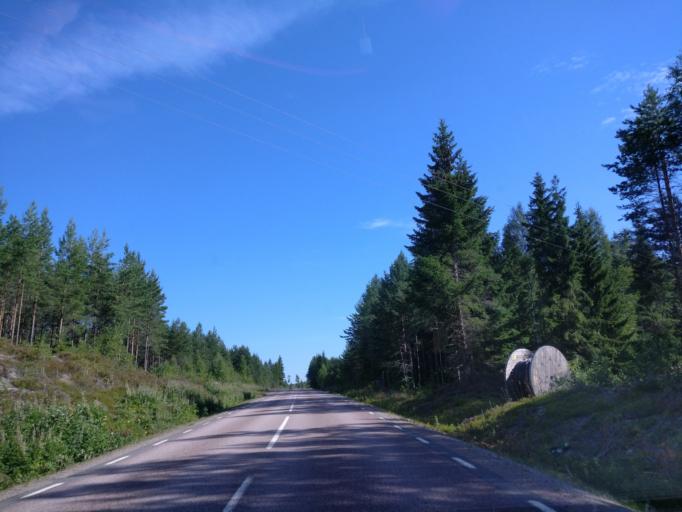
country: SE
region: Vaermland
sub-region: Hagfors Kommun
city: Hagfors
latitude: 60.0326
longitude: 13.9184
